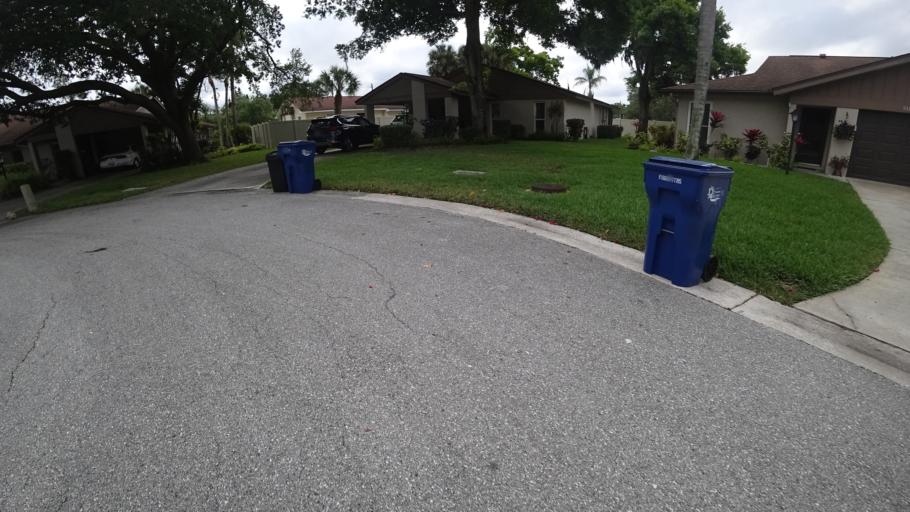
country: US
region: Florida
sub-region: Manatee County
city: South Bradenton
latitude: 27.4509
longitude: -82.5883
